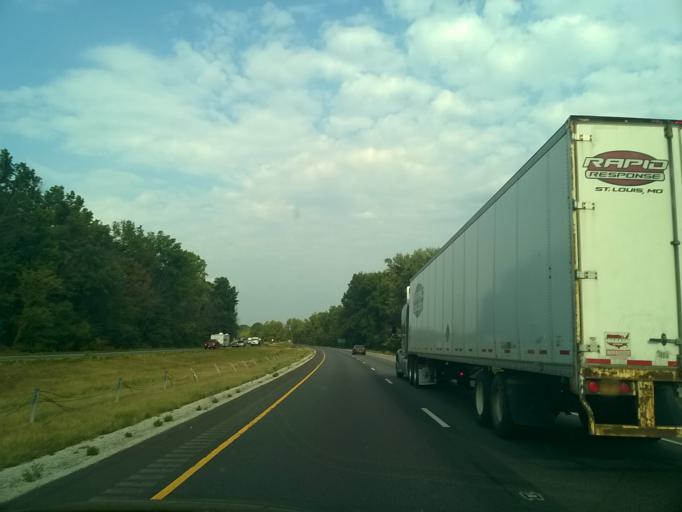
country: US
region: Indiana
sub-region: Clay County
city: Brazil
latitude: 39.4492
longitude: -87.1143
